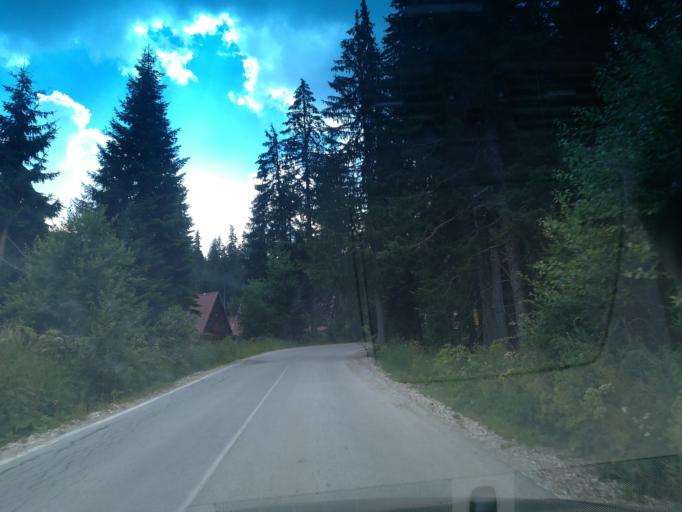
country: BG
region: Smolyan
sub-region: Obshtina Smolyan
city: Smolyan
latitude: 41.6534
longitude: 24.6875
